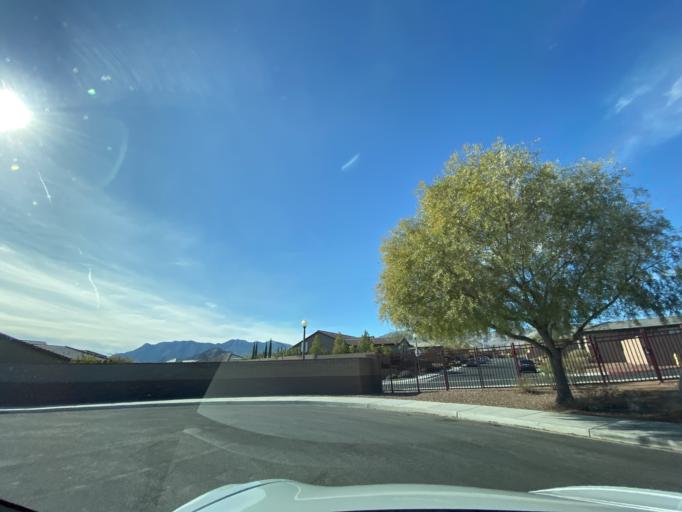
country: US
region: Nevada
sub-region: Clark County
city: Summerlin South
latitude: 36.2847
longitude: -115.3209
